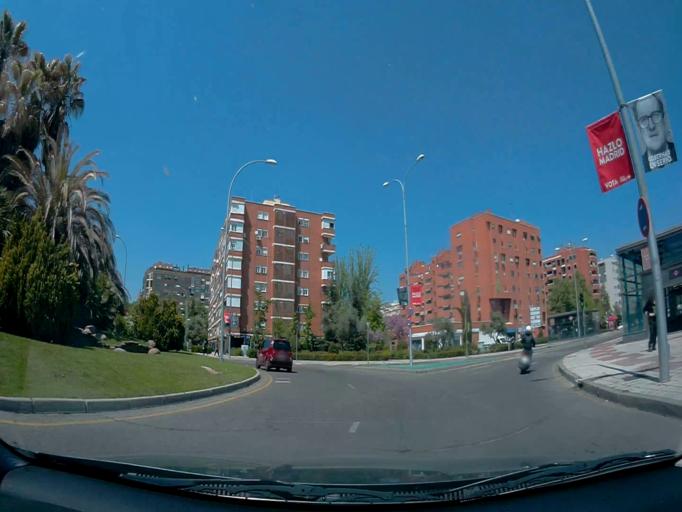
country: ES
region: Madrid
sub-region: Provincia de Madrid
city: Alcorcon
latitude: 40.3452
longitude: -3.8117
